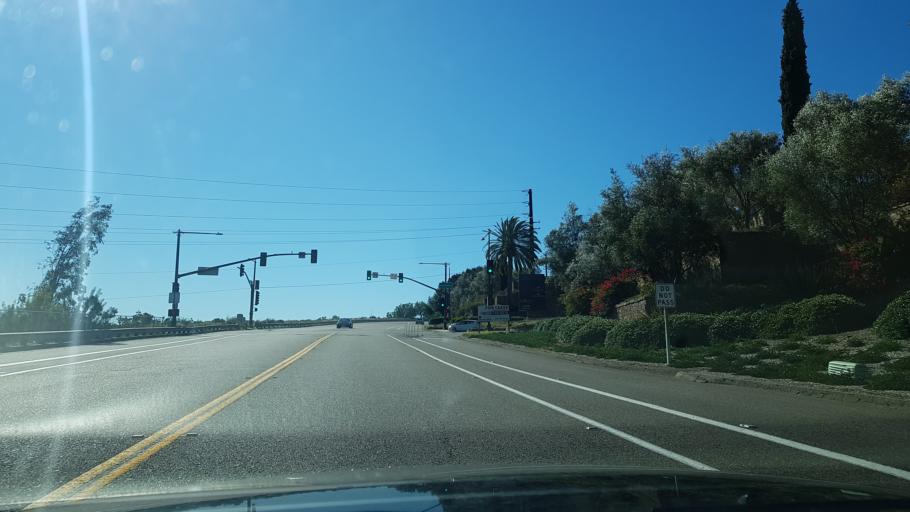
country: US
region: California
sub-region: San Diego County
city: Rancho Santa Fe
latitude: 33.0412
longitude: -117.1578
